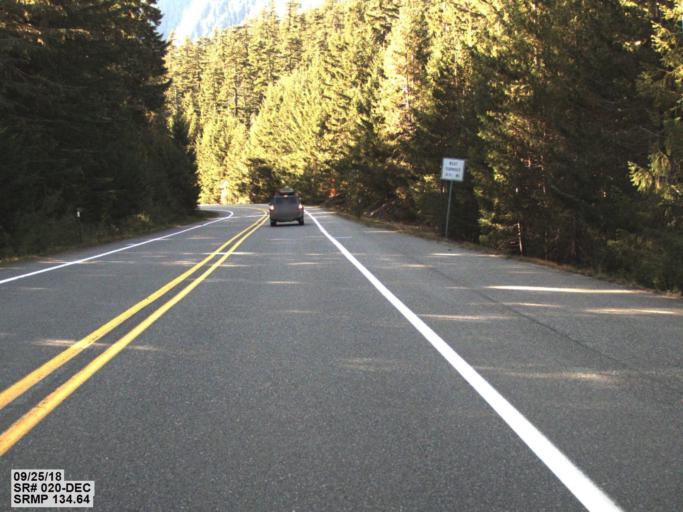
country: US
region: Washington
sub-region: Snohomish County
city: Darrington
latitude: 48.7285
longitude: -121.0508
